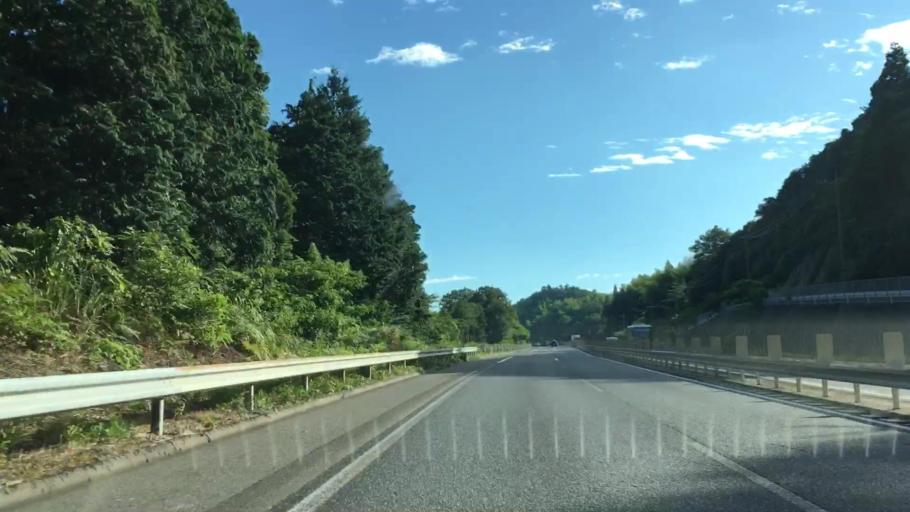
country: JP
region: Yamaguchi
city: Iwakuni
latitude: 34.1359
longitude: 132.1163
